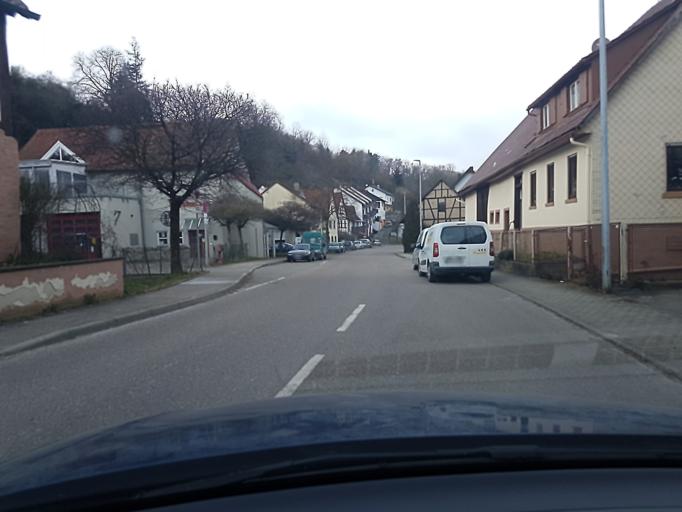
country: DE
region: Baden-Wuerttemberg
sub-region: Regierungsbezirk Stuttgart
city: Eberdingen
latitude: 48.8809
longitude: 8.9636
